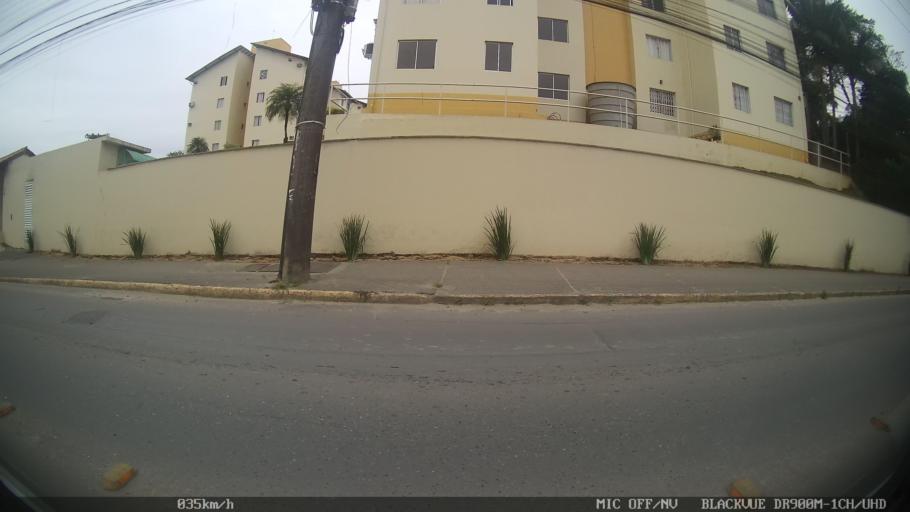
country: BR
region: Santa Catarina
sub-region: Joinville
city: Joinville
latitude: -26.3425
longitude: -48.7947
